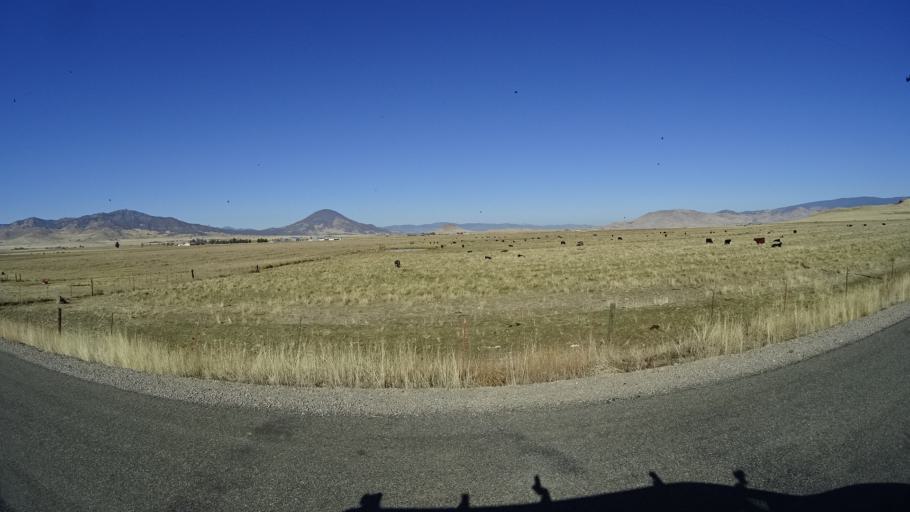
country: US
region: California
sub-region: Siskiyou County
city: Montague
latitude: 41.7559
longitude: -122.4726
